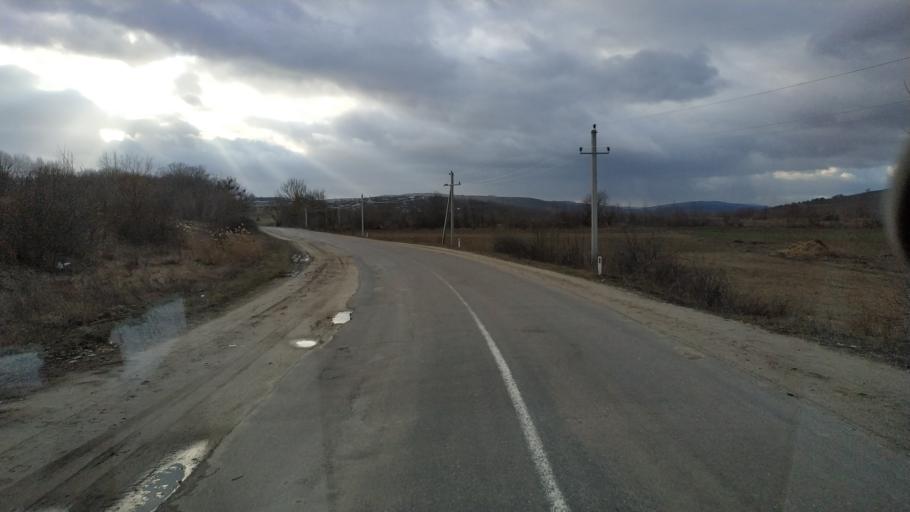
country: MD
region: Calarasi
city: Calarasi
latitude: 47.3107
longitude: 28.3746
